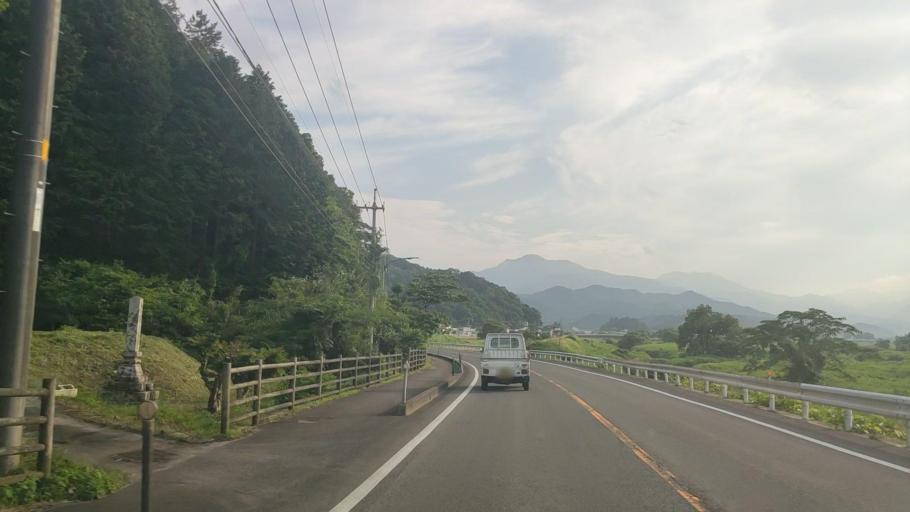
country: JP
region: Tottori
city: Kurayoshi
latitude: 35.3718
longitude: 133.7684
